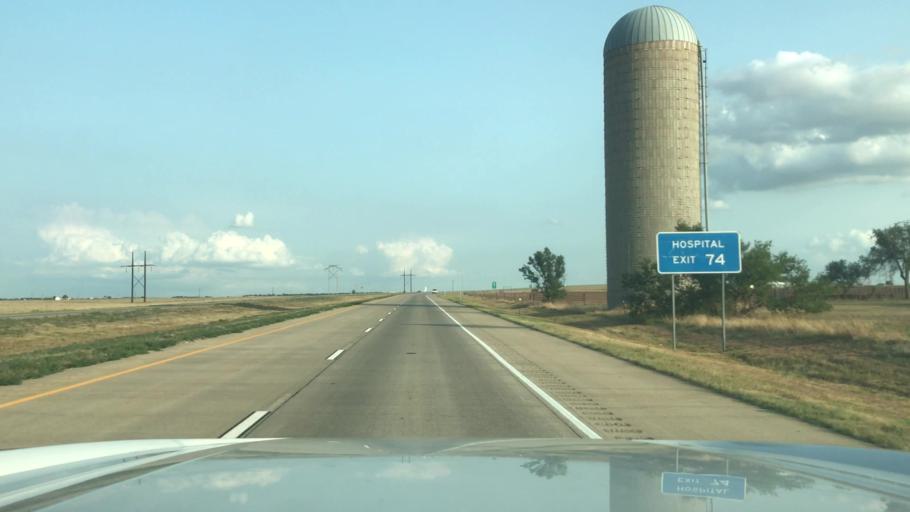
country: US
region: Texas
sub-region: Swisher County
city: Tulia
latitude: 34.5860
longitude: -101.7976
